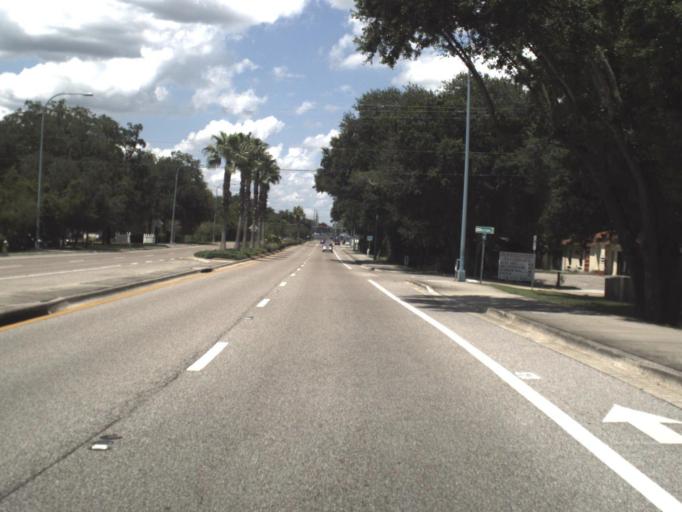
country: US
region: Florida
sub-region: Hillsborough County
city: Brandon
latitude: 27.9309
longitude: -82.3104
